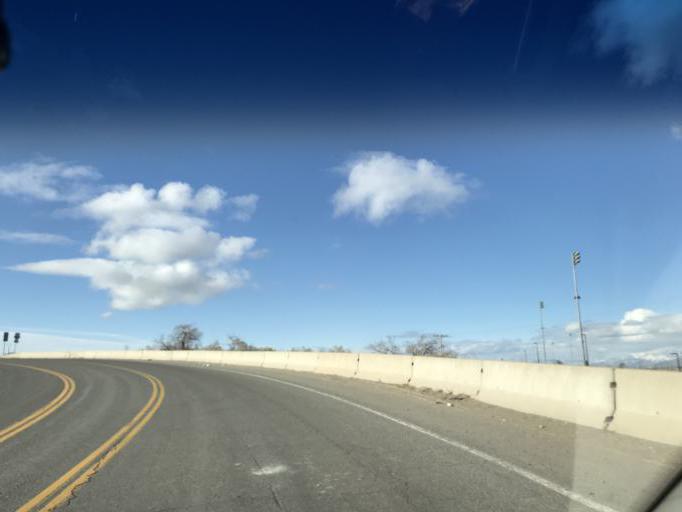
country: US
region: Utah
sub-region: Davis County
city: North Salt Lake
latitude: 40.8126
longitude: -111.9474
